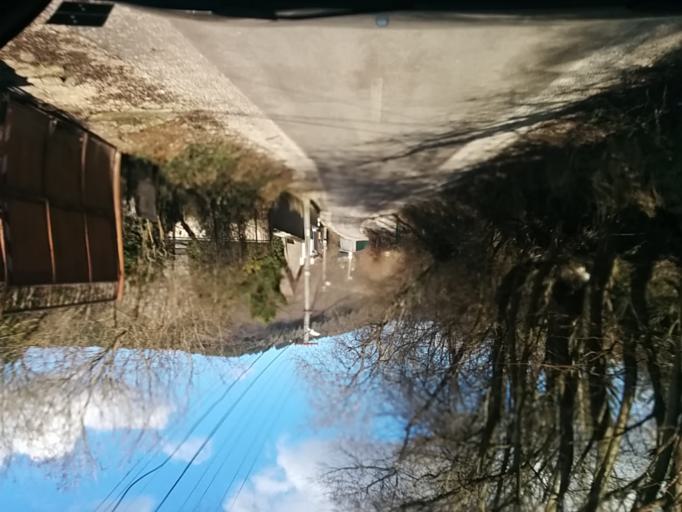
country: SK
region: Nitriansky
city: Cachtice
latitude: 48.7182
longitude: 17.7859
